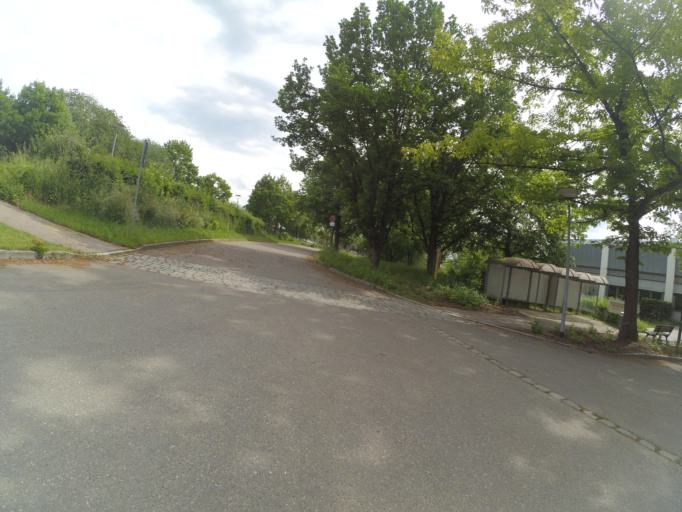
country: DE
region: Bavaria
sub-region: Swabia
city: Guenzburg
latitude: 48.4593
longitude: 10.2954
